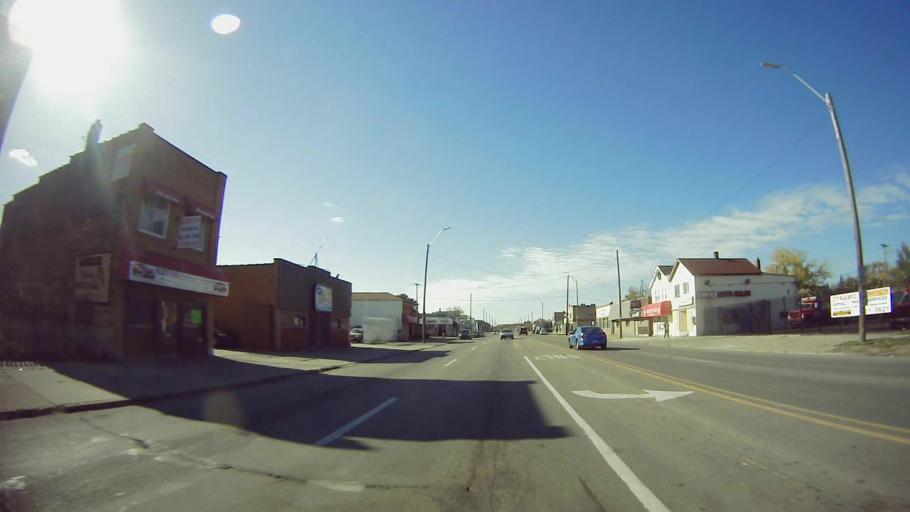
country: US
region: Michigan
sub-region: Wayne County
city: Dearborn Heights
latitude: 42.3432
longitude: -83.2307
